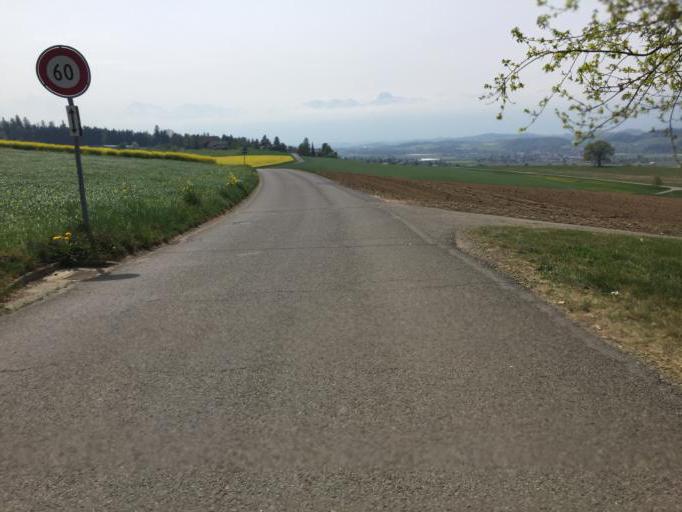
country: CH
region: Bern
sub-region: Bern-Mittelland District
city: Niederwichtrach
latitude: 46.8611
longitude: 7.5815
